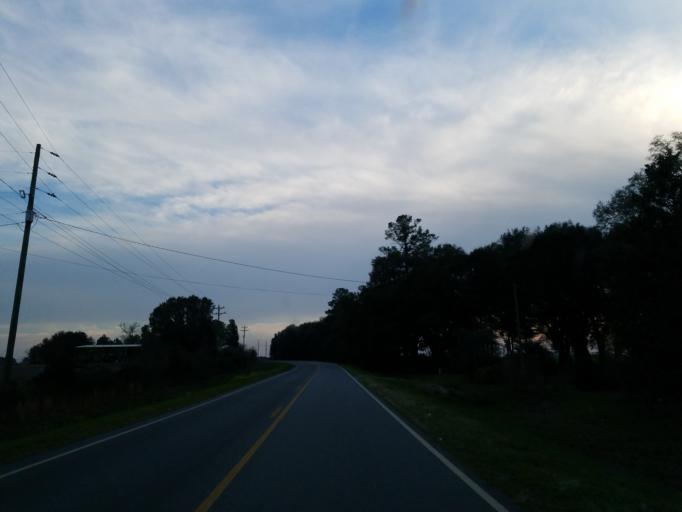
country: US
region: Georgia
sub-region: Tift County
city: Omega
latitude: 31.2446
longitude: -83.5805
